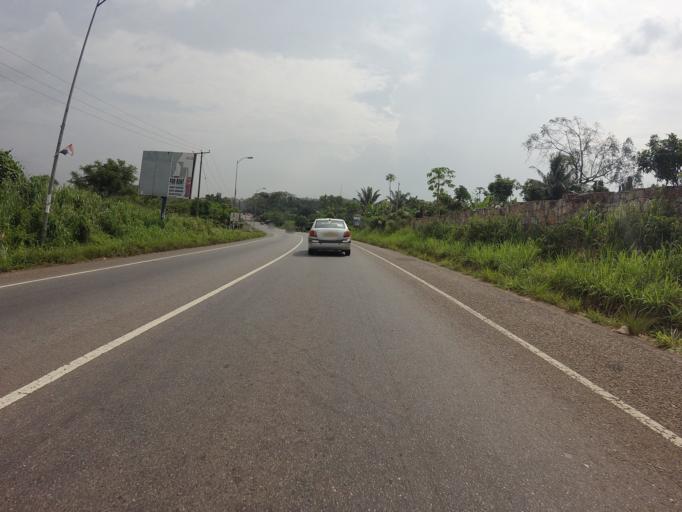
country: GH
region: Eastern
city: Aburi
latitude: 5.8234
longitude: -0.1863
